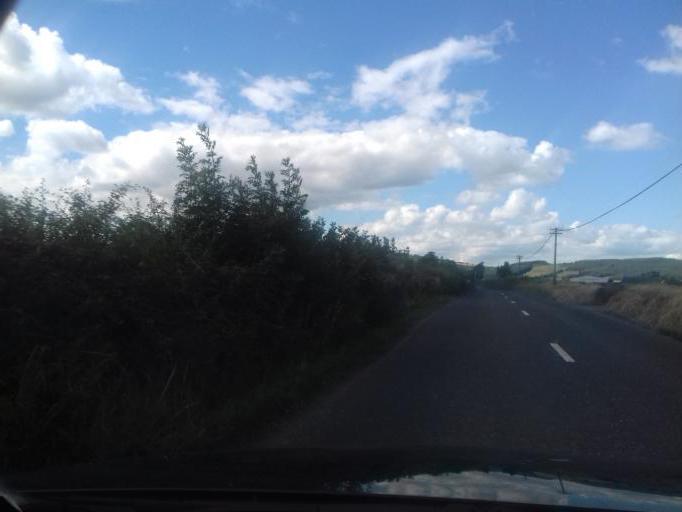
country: IE
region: Munster
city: Carrick-on-Suir
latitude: 52.3793
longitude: -7.4555
